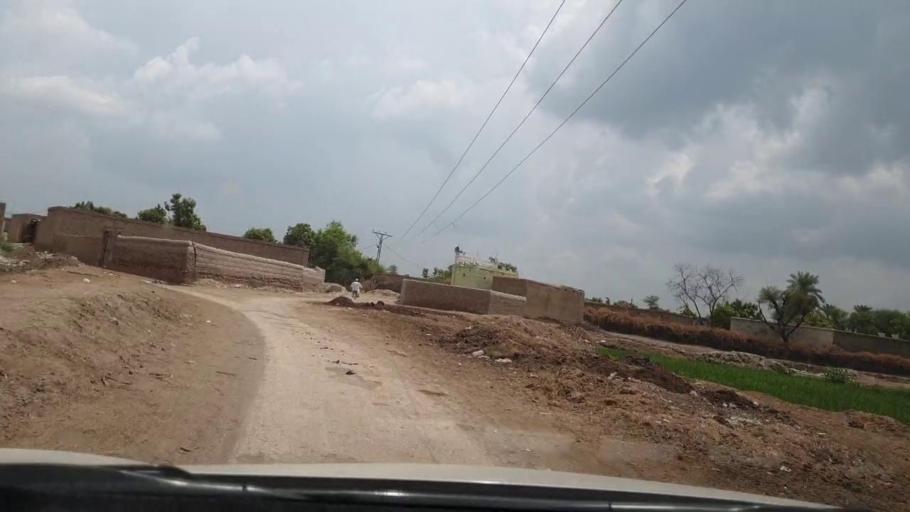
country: PK
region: Sindh
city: Goth Garelo
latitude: 27.4206
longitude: 68.1157
